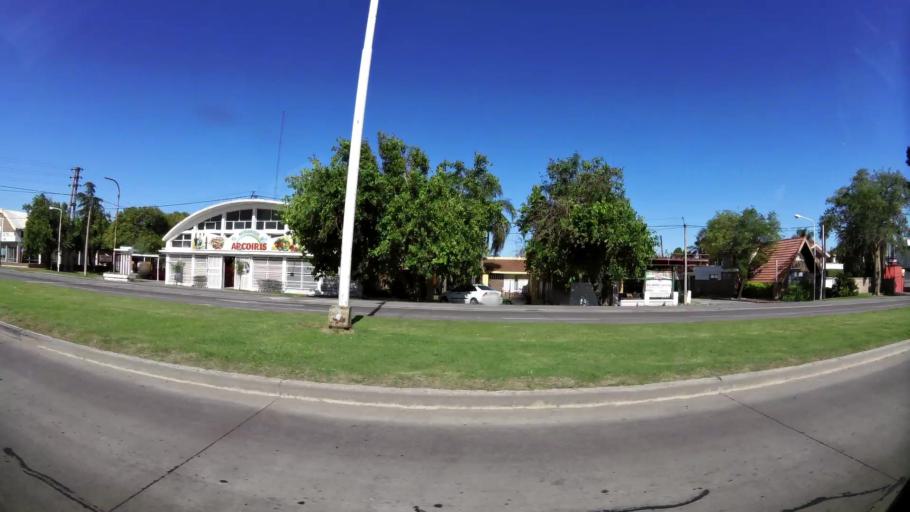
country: AR
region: Santa Fe
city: Rafaela
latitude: -31.2540
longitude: -61.5058
